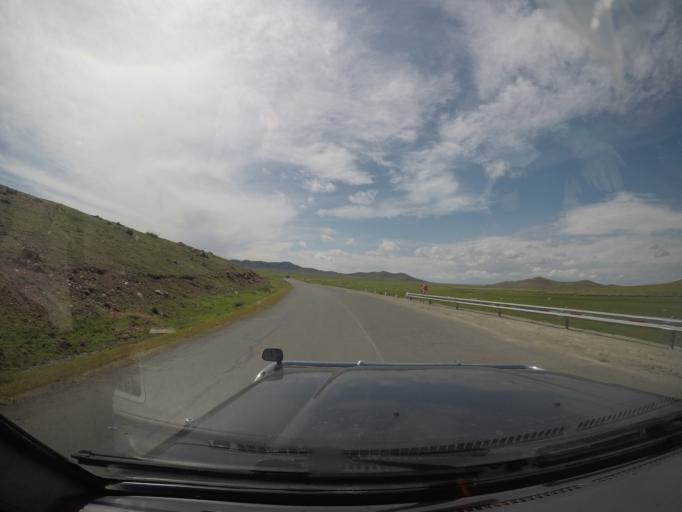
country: MN
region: Hentiy
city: Moron
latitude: 47.3976
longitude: 110.2877
